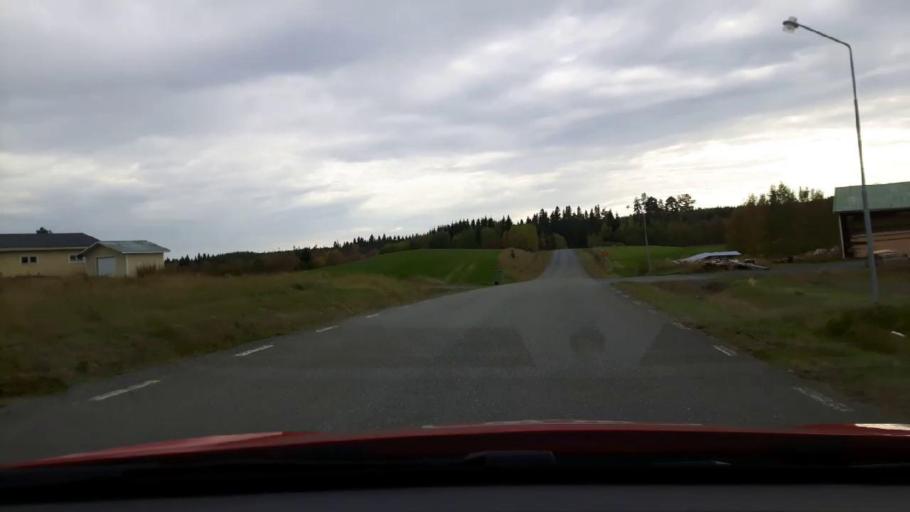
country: SE
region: Jaemtland
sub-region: Krokoms Kommun
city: Krokom
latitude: 63.2253
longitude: 14.1339
